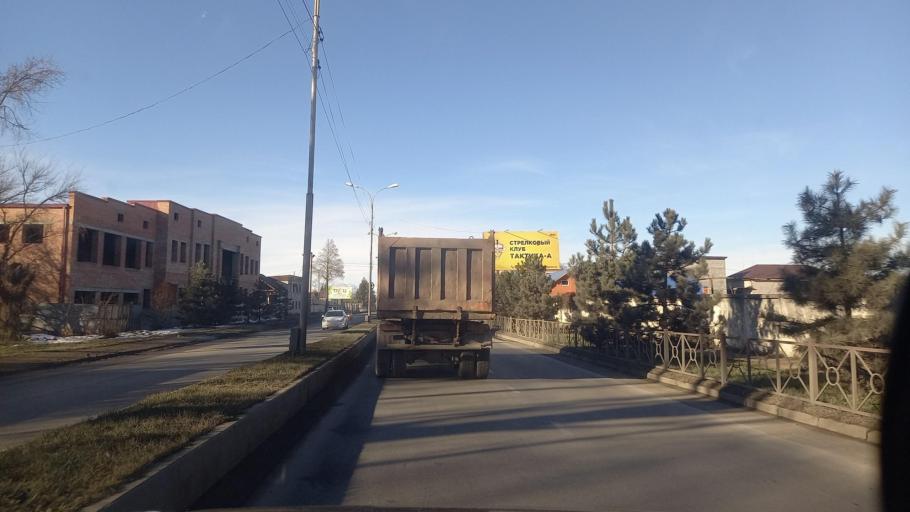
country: RU
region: North Ossetia
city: Vladikavkaz
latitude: 43.0255
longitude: 44.6399
